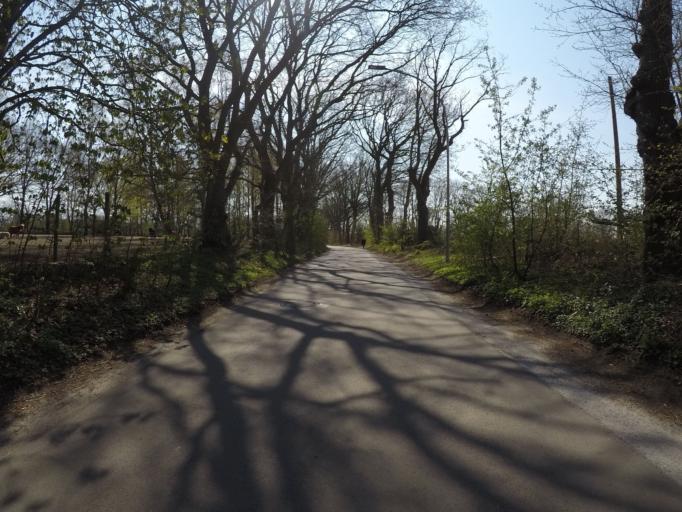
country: DE
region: Schleswig-Holstein
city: Rellingen
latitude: 53.5994
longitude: 9.8113
